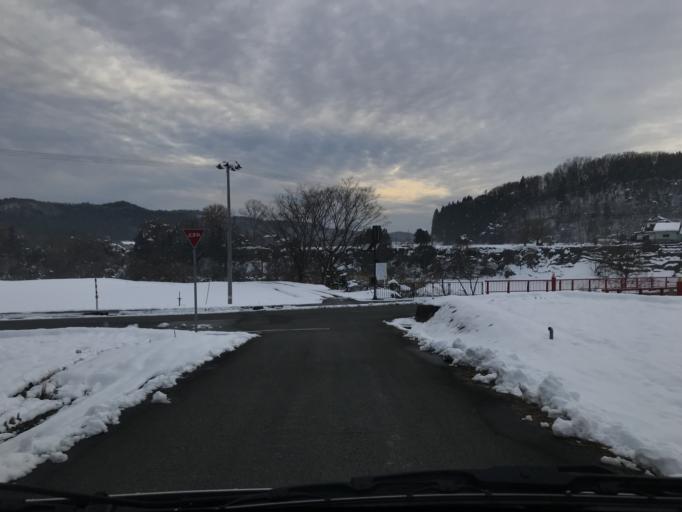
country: JP
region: Iwate
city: Mizusawa
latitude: 39.0406
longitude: 141.0577
